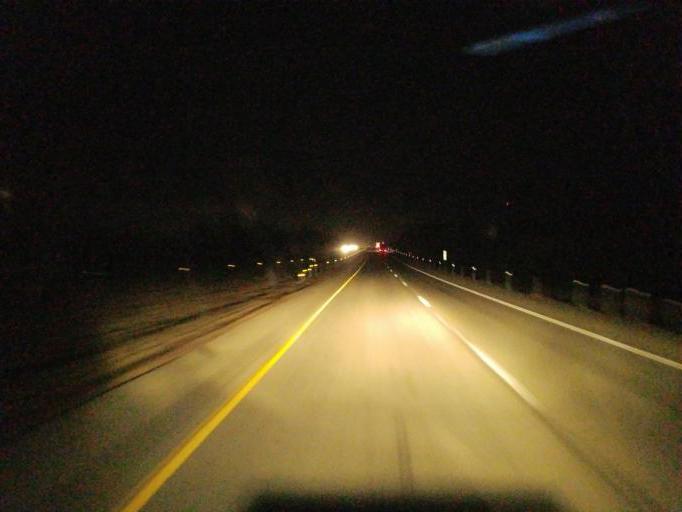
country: US
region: Iowa
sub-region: Madison County
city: Earlham
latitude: 41.5177
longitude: -94.1444
